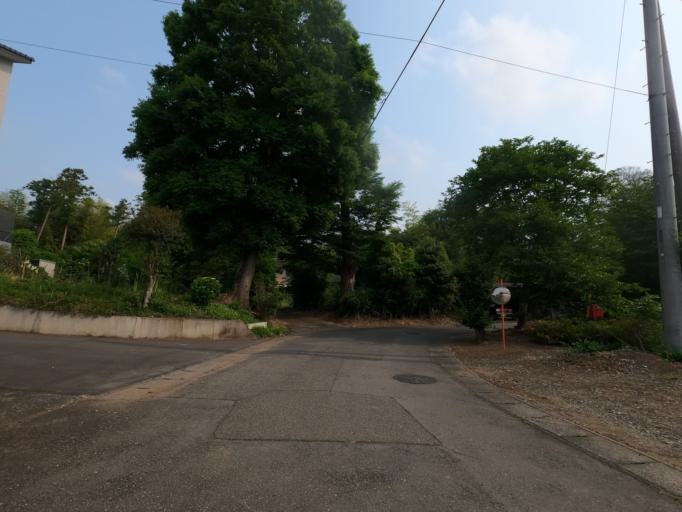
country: JP
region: Ibaraki
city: Moriya
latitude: 35.9622
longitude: 139.9512
